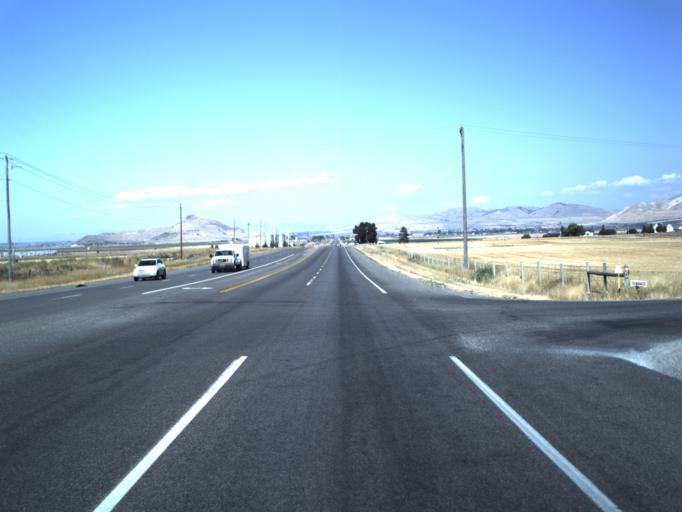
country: US
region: Utah
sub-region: Cache County
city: Richmond
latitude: 41.9632
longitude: -111.8128
